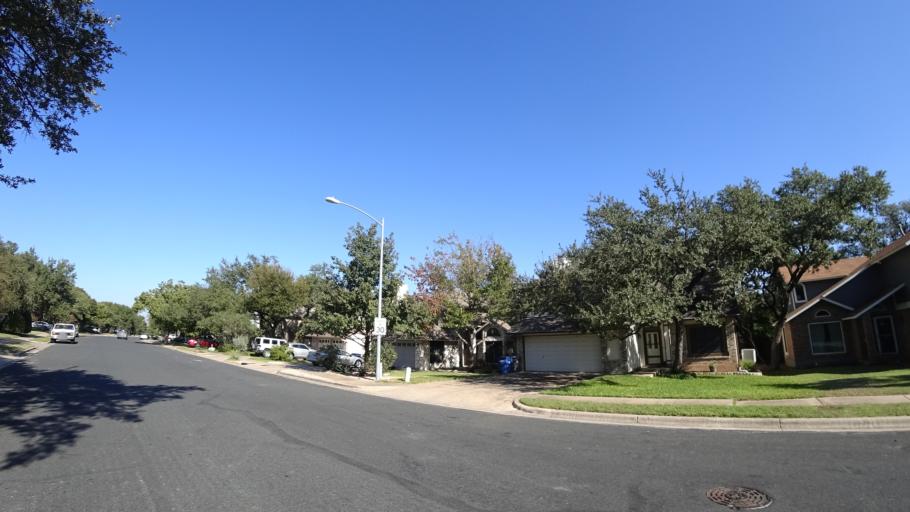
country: US
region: Texas
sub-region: Travis County
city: Shady Hollow
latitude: 30.1977
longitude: -97.8488
